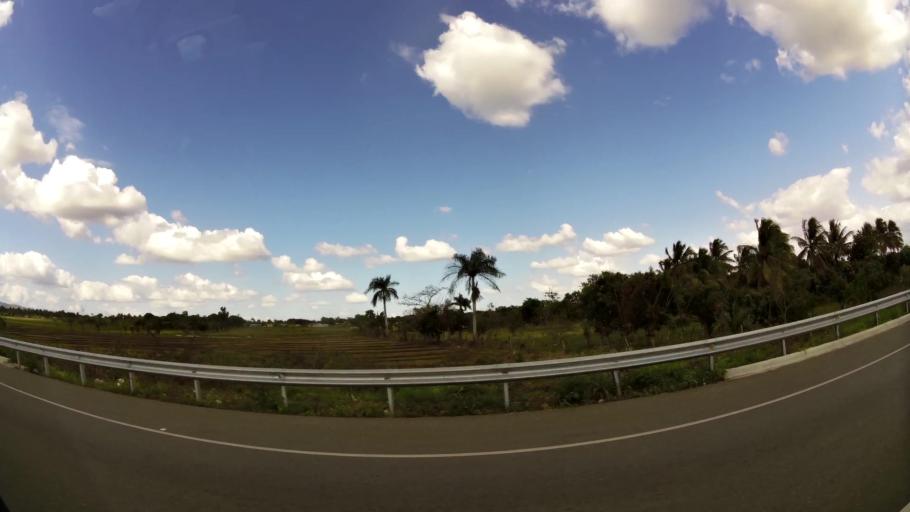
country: DO
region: Santo Domingo
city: Santo Domingo Oeste
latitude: 18.5315
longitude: -70.0708
